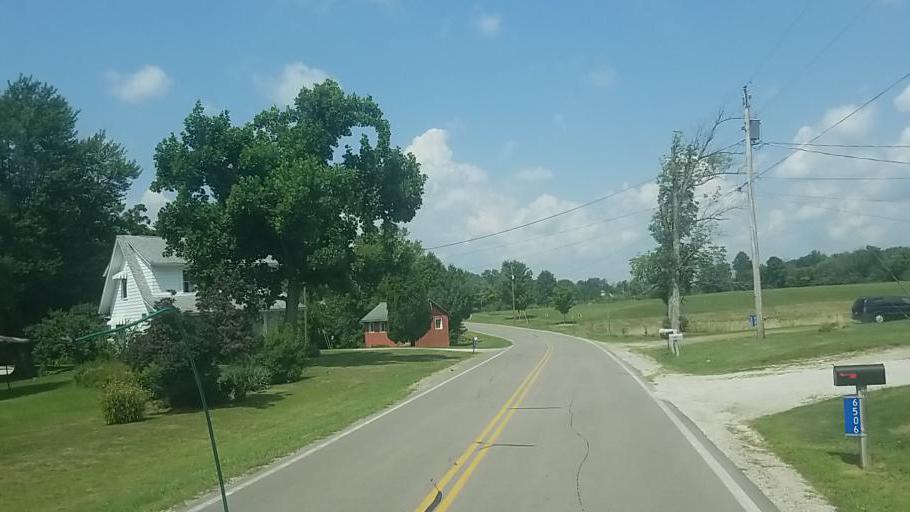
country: US
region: Ohio
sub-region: Crawford County
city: Galion
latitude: 40.8010
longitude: -82.8044
